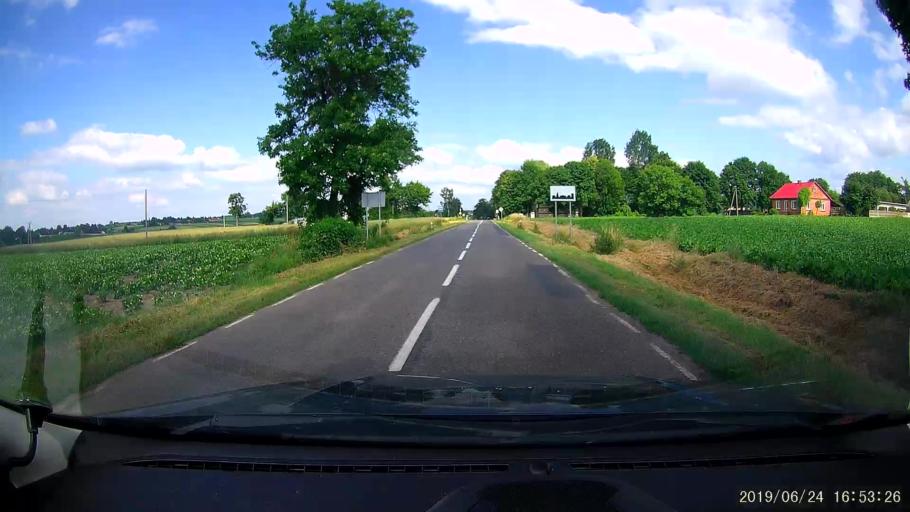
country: PL
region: Lublin Voivodeship
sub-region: Powiat tomaszowski
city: Telatyn
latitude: 50.5354
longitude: 23.8012
